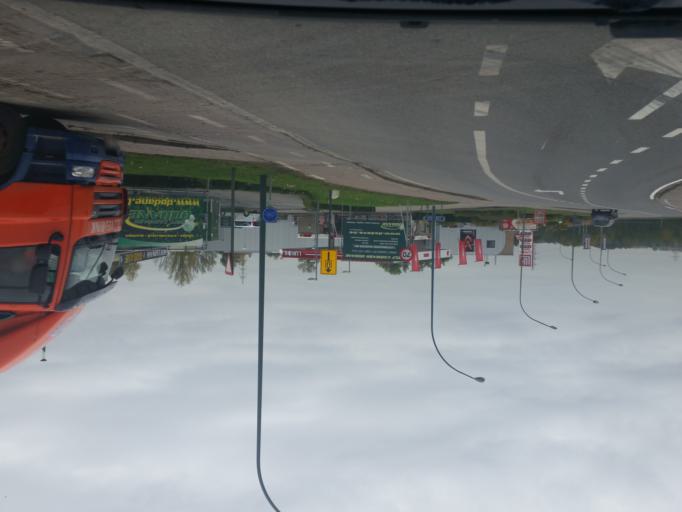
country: BE
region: Flanders
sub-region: Provincie Vlaams-Brabant
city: Halle
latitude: 50.7523
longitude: 4.2554
